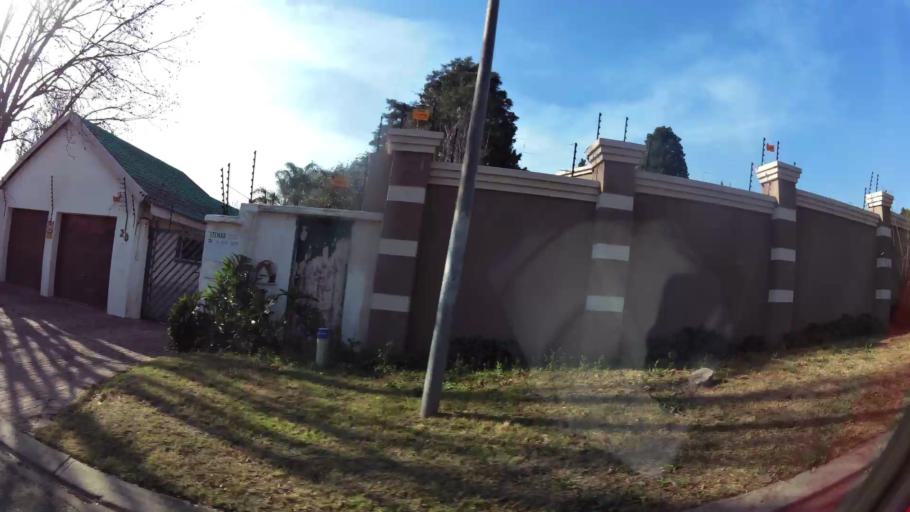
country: ZA
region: Gauteng
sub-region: City of Johannesburg Metropolitan Municipality
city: Roodepoort
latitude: -26.0952
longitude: 27.9715
